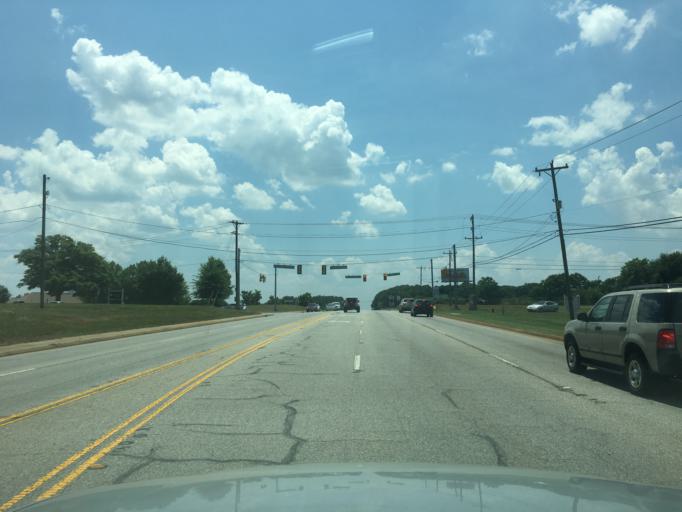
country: US
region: South Carolina
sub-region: Anderson County
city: Northlake
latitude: 34.5777
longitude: -82.6227
